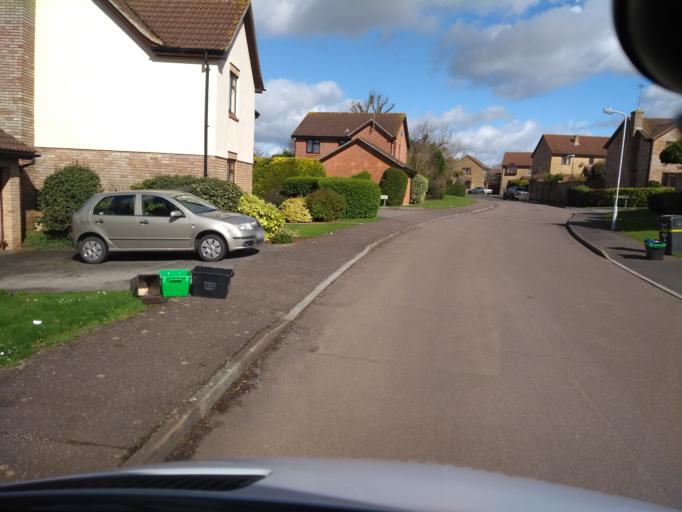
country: GB
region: England
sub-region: Somerset
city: Taunton
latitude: 50.9993
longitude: -3.0897
